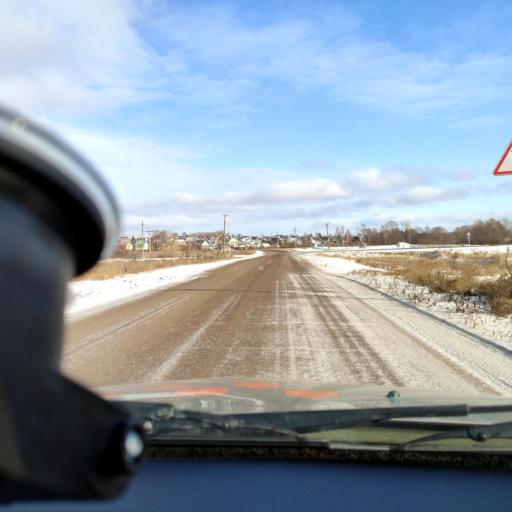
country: RU
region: Bashkortostan
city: Mikhaylovka
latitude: 54.7968
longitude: 55.7775
